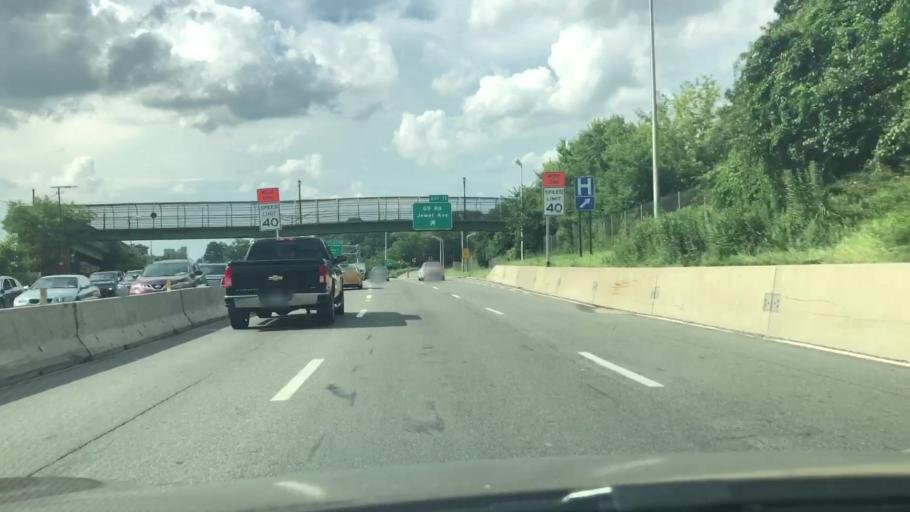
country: US
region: New York
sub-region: Queens County
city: Jamaica
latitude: 40.7223
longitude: -73.8271
